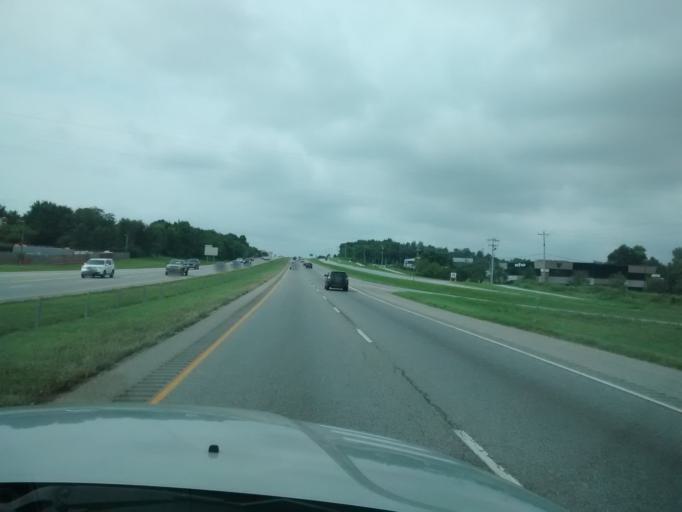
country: US
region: Arkansas
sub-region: Washington County
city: Johnson
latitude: 36.1038
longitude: -94.1819
